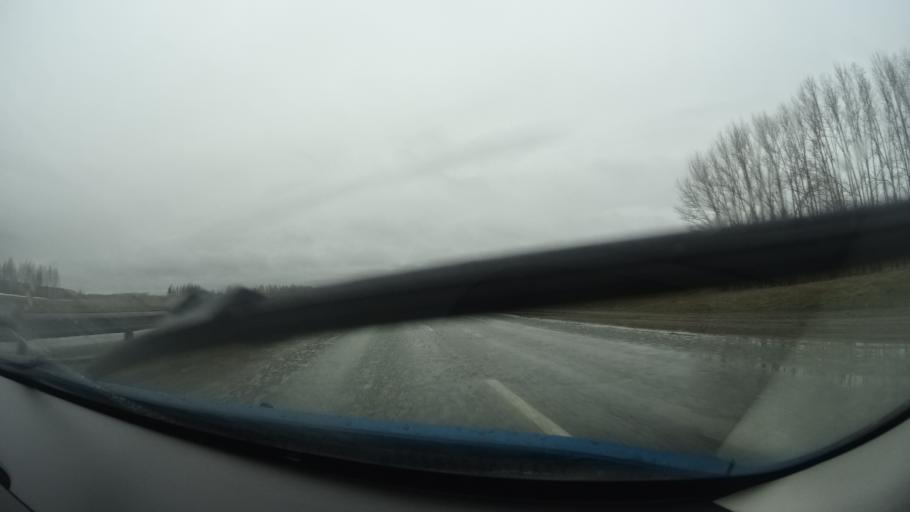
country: RU
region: Bashkortostan
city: Dmitriyevka
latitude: 54.6778
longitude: 55.3453
